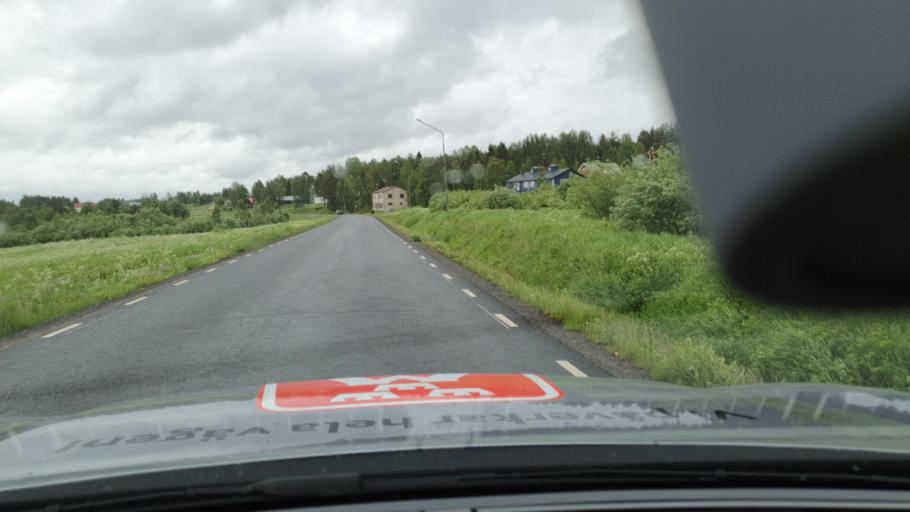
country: FI
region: Lapland
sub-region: Torniolaakso
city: Ylitornio
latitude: 66.1772
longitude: 23.7925
